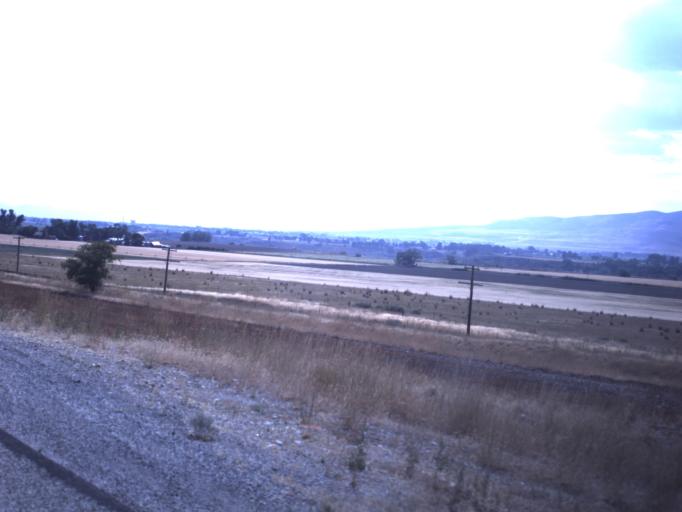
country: US
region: Utah
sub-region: Box Elder County
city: Garland
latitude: 41.7817
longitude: -112.0929
